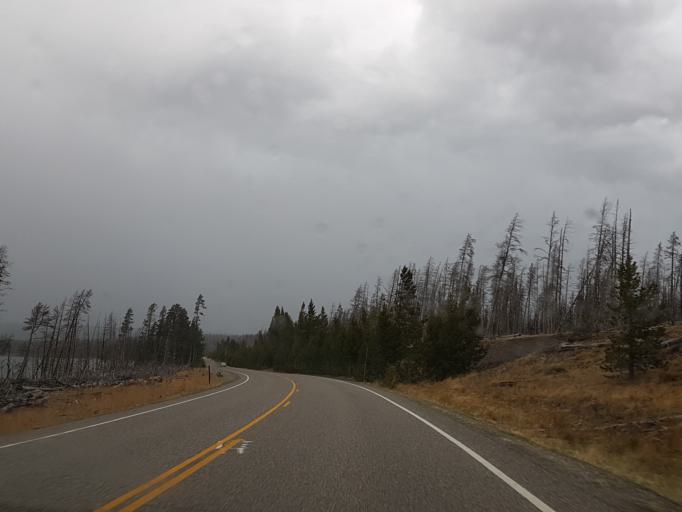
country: US
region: Montana
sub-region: Gallatin County
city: West Yellowstone
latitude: 44.4695
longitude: -110.5183
